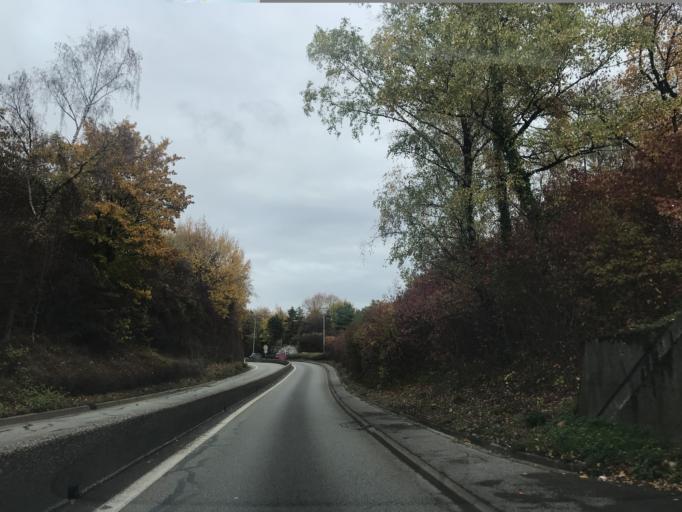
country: FR
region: Rhone-Alpes
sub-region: Departement de la Haute-Savoie
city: Annecy-le-Vieux
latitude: 45.9251
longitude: 6.1254
